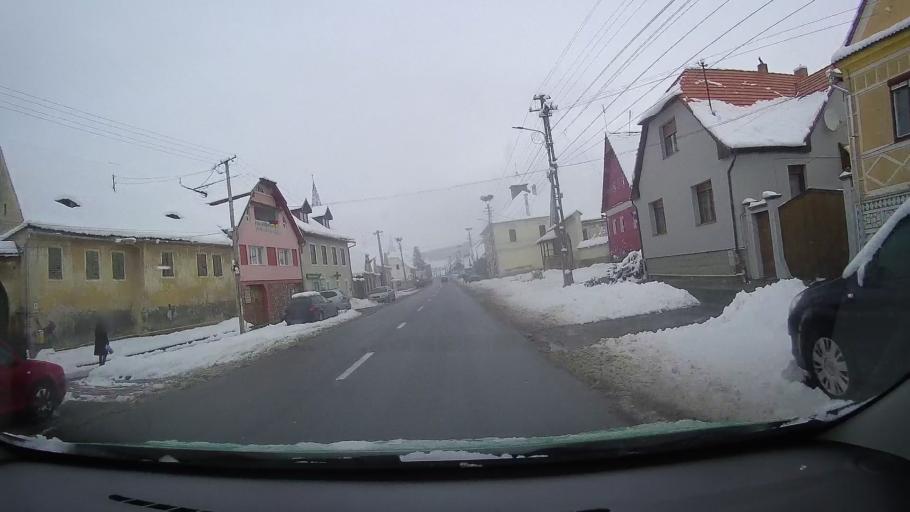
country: RO
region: Sibiu
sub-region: Comuna Cristian
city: Cristian
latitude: 45.7824
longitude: 24.0280
